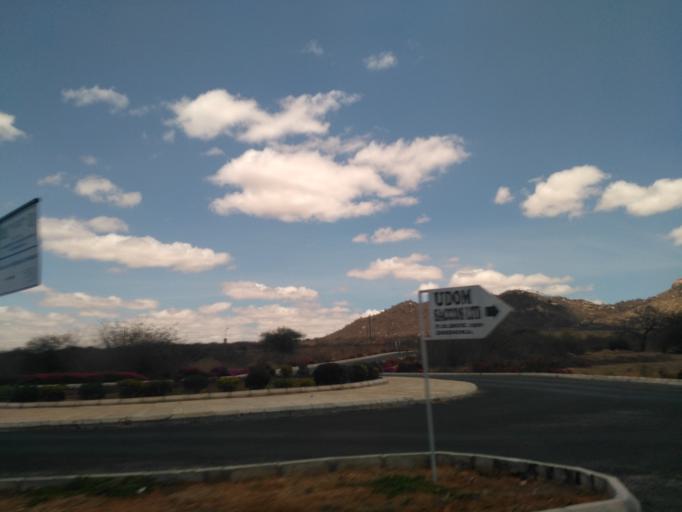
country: TZ
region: Dodoma
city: Kisasa
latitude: -6.2179
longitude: 35.8100
